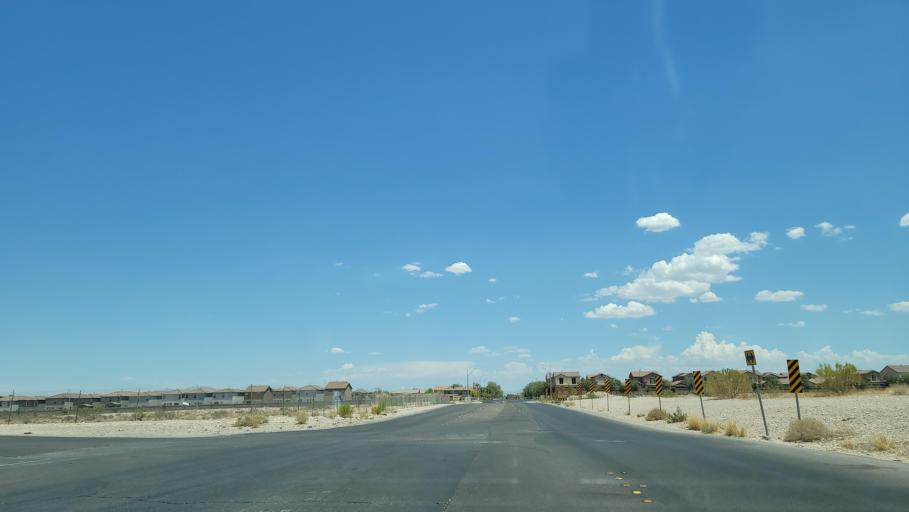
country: US
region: Nevada
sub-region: Clark County
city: Spring Valley
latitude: 36.0777
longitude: -115.2728
